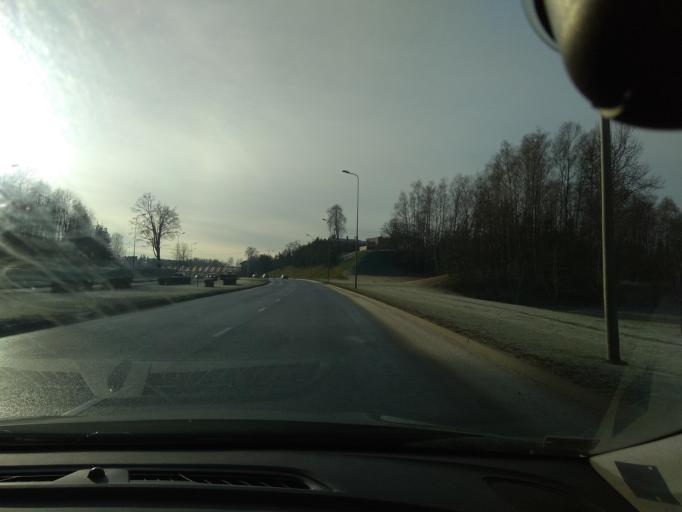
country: LT
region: Vilnius County
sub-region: Vilnius
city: Fabijoniskes
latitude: 54.7488
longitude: 25.2645
